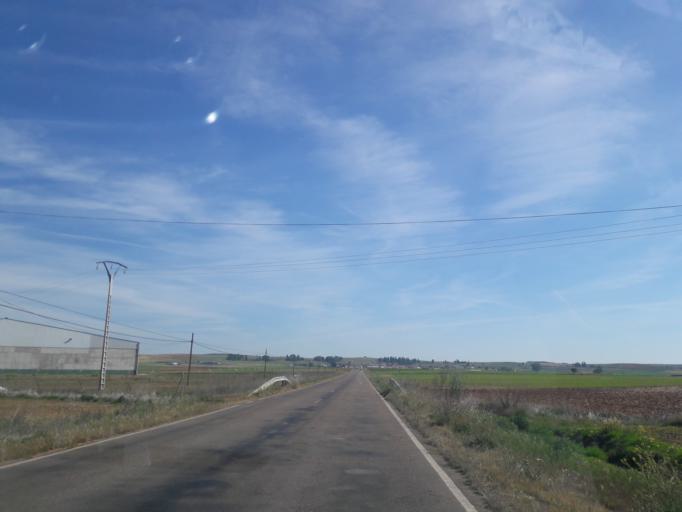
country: ES
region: Castille and Leon
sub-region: Provincia de Salamanca
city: Babilafuente
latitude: 40.9880
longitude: -5.4061
